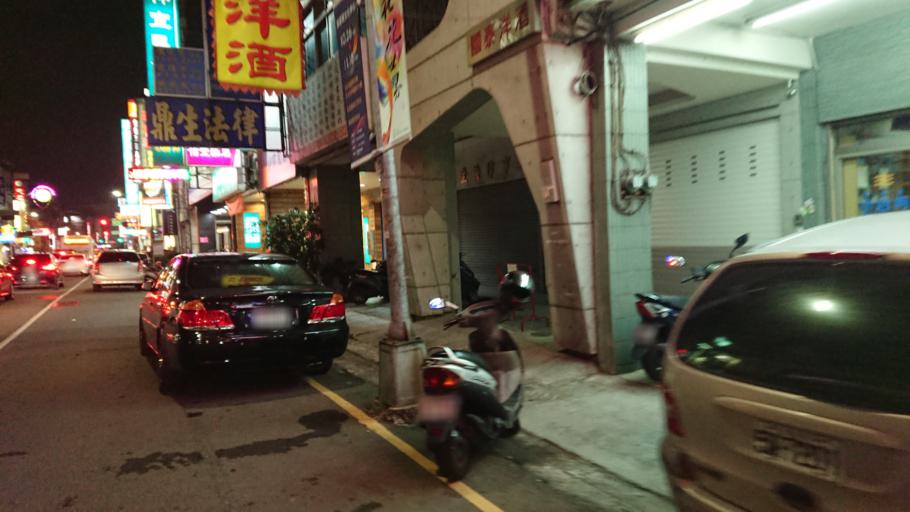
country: TW
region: Taiwan
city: Fengyuan
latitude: 24.2505
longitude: 120.7147
